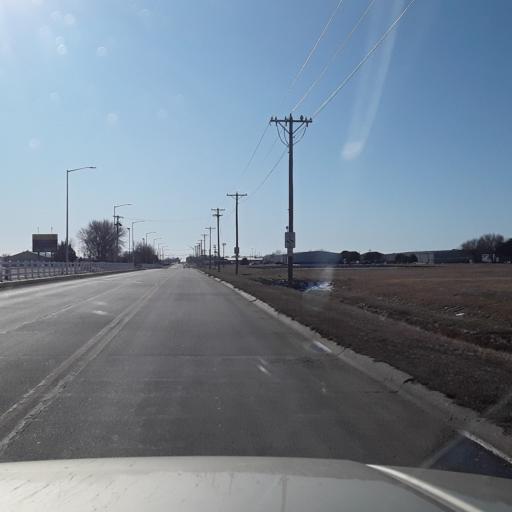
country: US
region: Nebraska
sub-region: Adams County
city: Hastings
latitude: 40.5735
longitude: -98.4021
